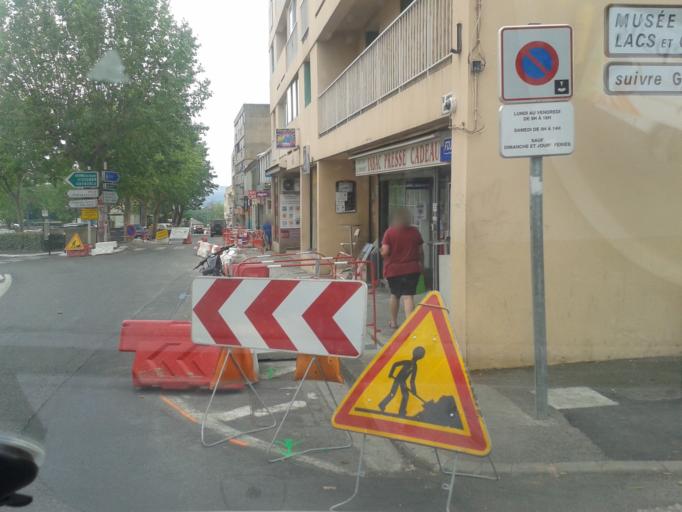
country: FR
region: Provence-Alpes-Cote d'Azur
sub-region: Departement des Alpes-de-Haute-Provence
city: Manosque
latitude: 43.8281
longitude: 5.7863
